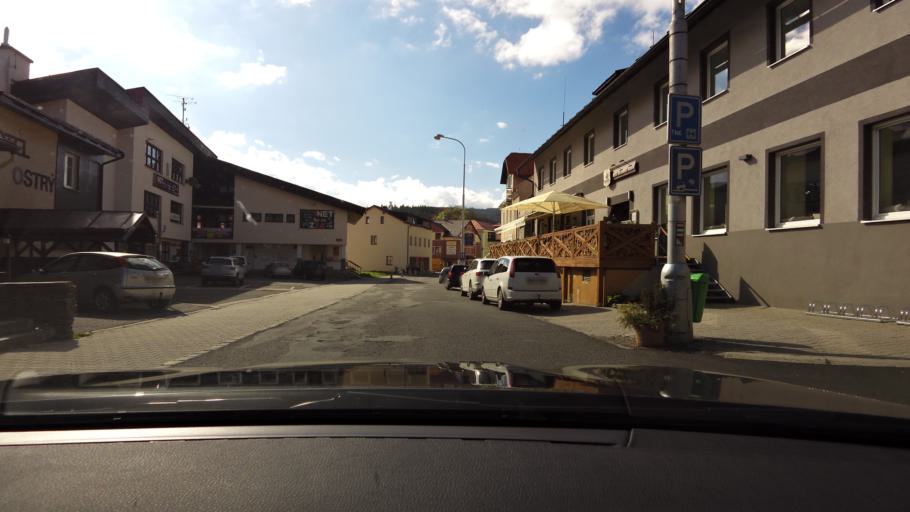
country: CZ
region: Plzensky
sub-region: Okres Klatovy
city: Zelezna Ruda
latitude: 49.1377
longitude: 13.2322
